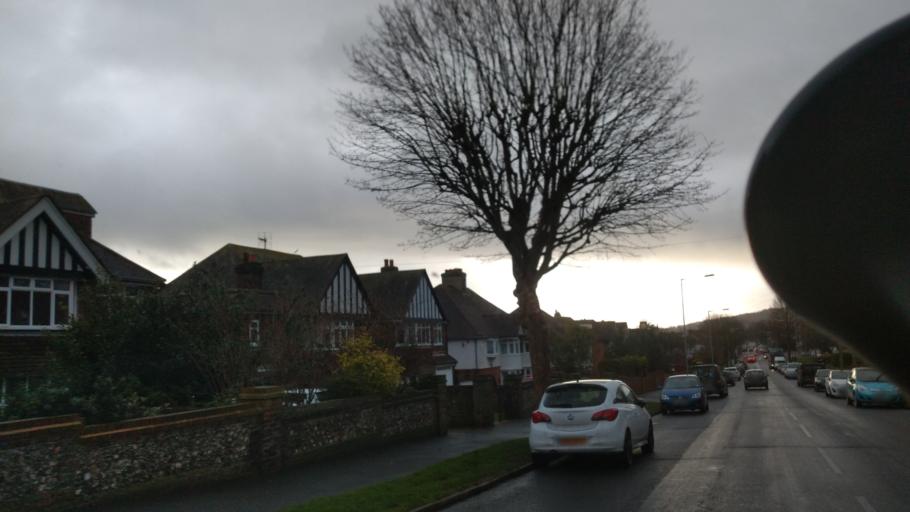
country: GB
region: England
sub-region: East Sussex
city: Eastbourne
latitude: 50.7821
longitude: 0.2547
